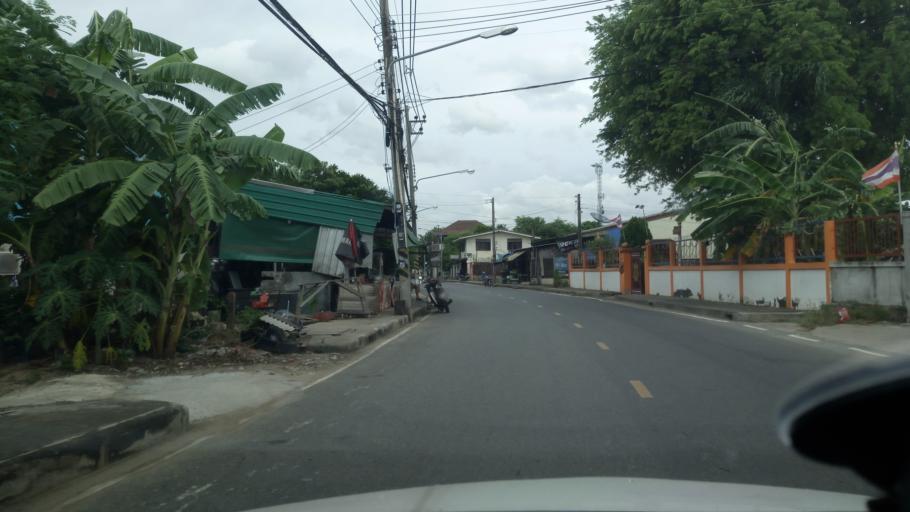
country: TH
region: Chon Buri
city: Phanat Nikhom
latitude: 13.4559
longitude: 101.1783
